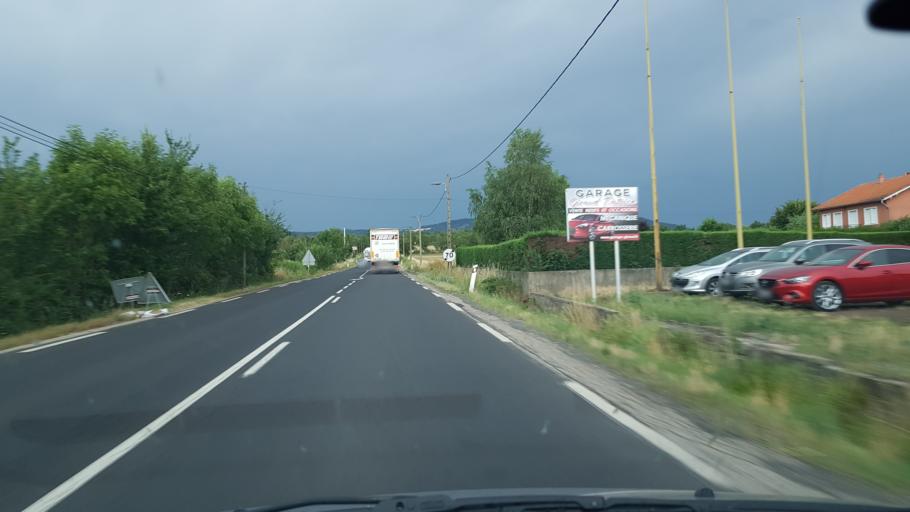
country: FR
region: Auvergne
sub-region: Departement de la Haute-Loire
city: Paulhaguet
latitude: 45.1510
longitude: 3.5468
